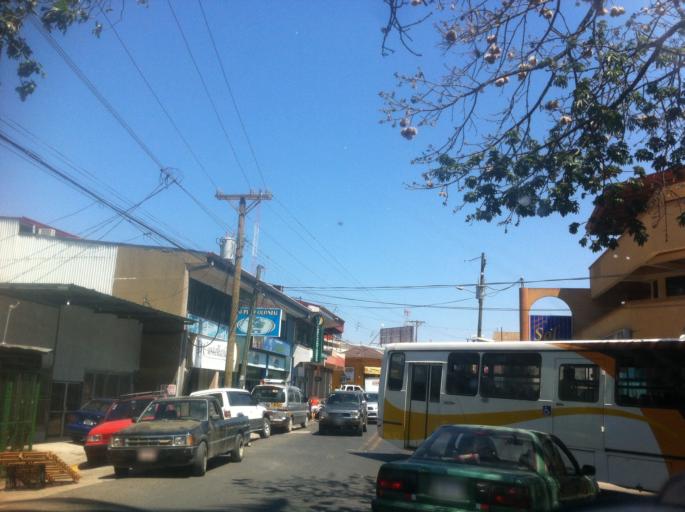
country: CR
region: Guanacaste
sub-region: Canton de Nicoya
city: Nicoya
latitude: 10.1343
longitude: -85.4458
